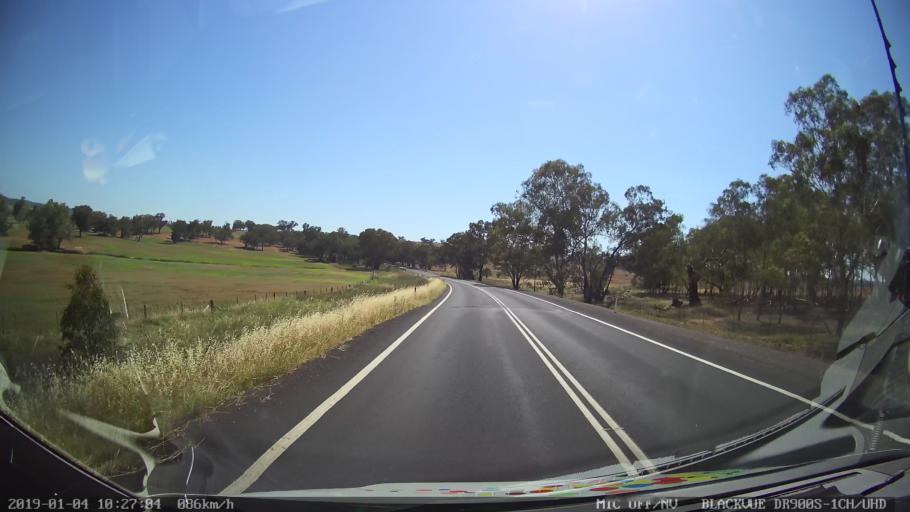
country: AU
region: New South Wales
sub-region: Cabonne
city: Canowindra
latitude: -33.3737
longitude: 148.5946
